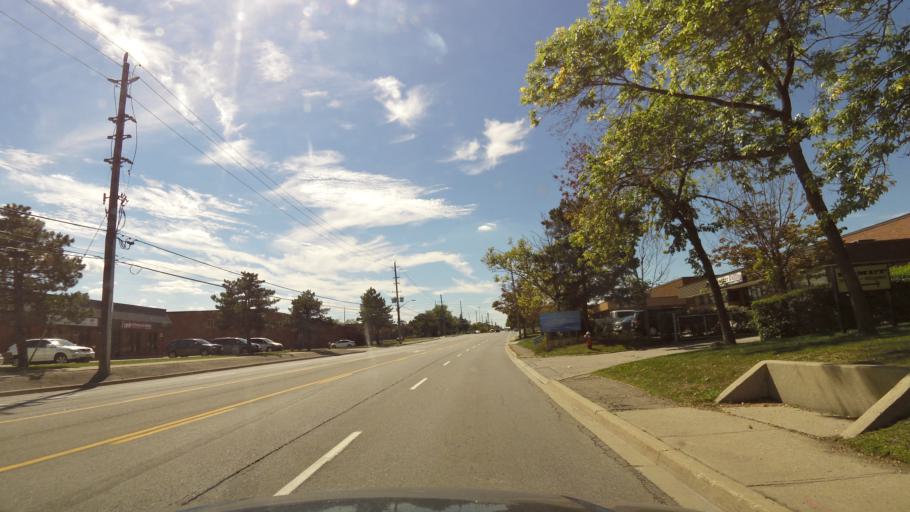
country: CA
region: Ontario
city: Mississauga
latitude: 43.6347
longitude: -79.6391
